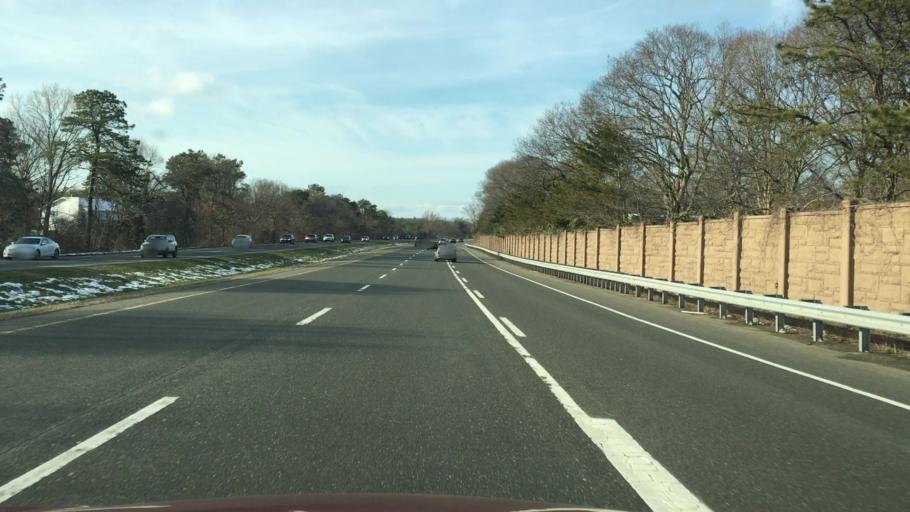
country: US
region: New York
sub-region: Suffolk County
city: Centereach
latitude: 40.8638
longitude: -73.0691
